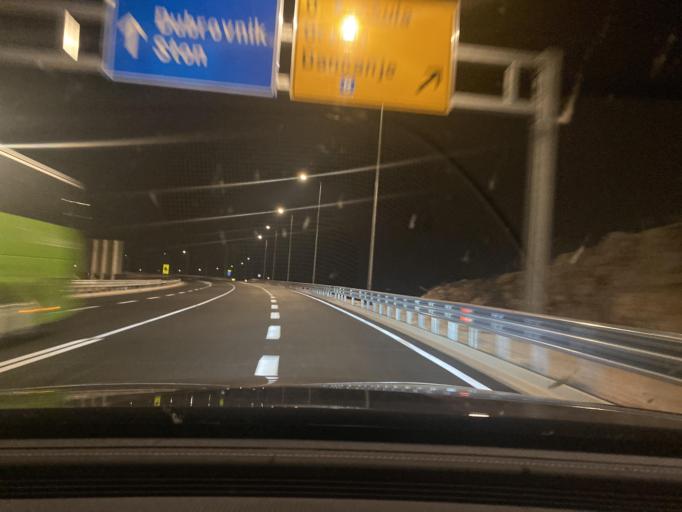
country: BA
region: Federation of Bosnia and Herzegovina
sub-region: Hercegovacko-Bosanski Kanton
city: Neum
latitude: 42.8684
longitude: 17.5644
